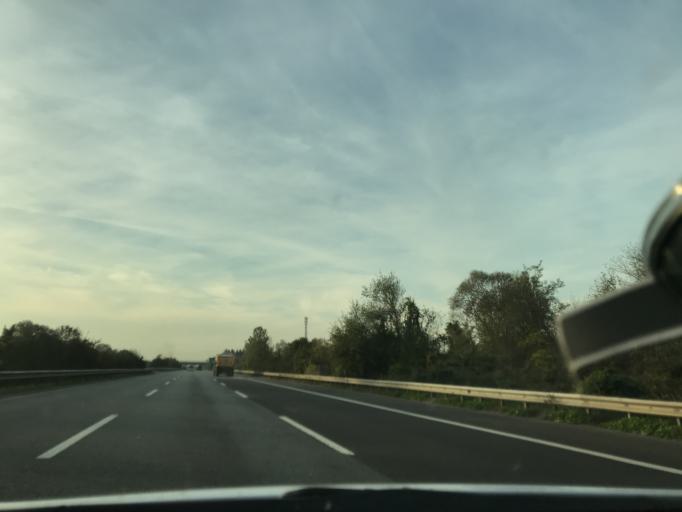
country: TR
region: Duzce
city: Cilimli
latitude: 40.8242
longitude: 31.0608
